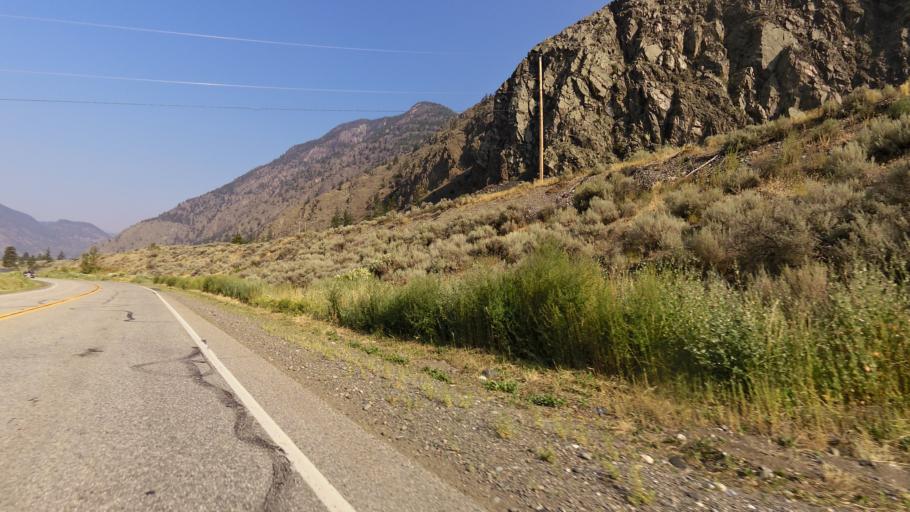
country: CA
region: British Columbia
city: Oliver
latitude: 49.2173
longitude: -119.9159
